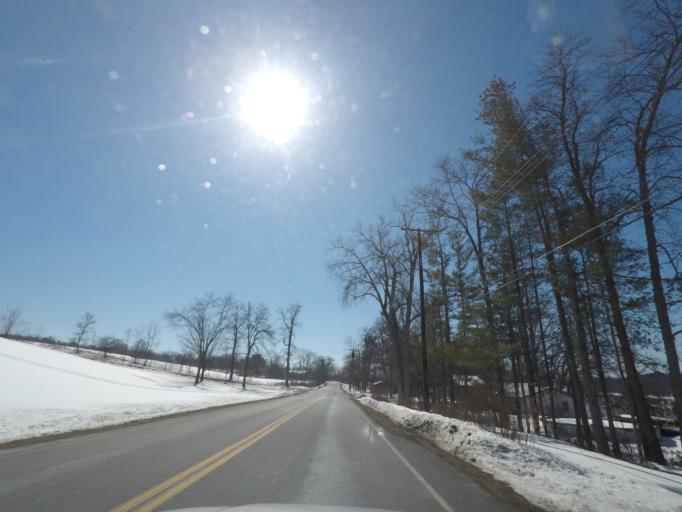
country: US
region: New York
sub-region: Saratoga County
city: Schuylerville
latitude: 43.0800
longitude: -73.5746
